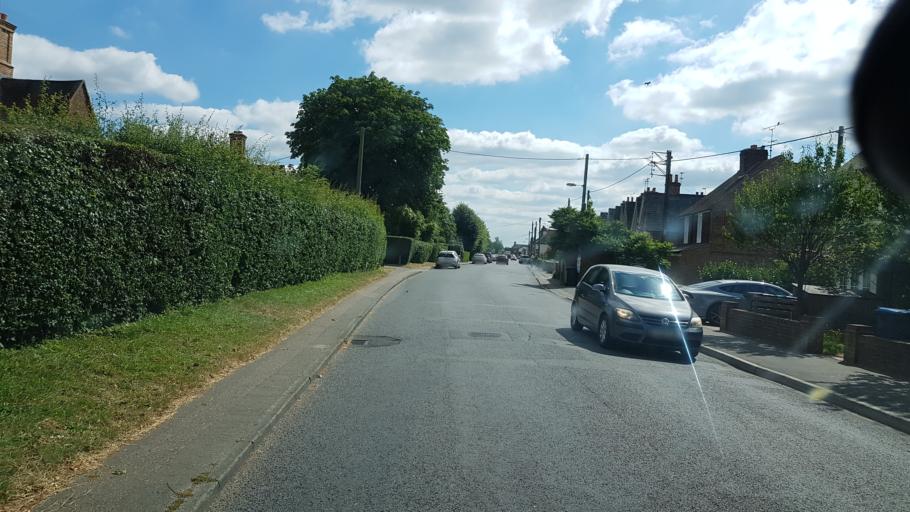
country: GB
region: England
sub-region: West Sussex
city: Broadfield
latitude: 51.0562
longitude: -0.1987
